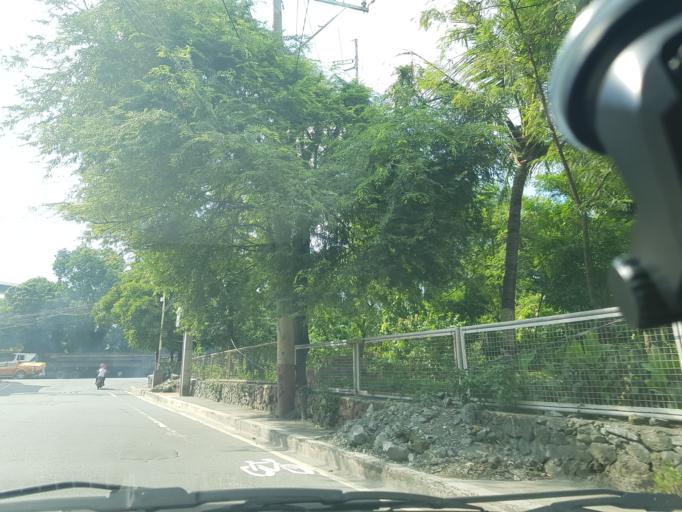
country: PH
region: Metro Manila
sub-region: Marikina
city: Calumpang
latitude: 14.5966
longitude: 121.0904
